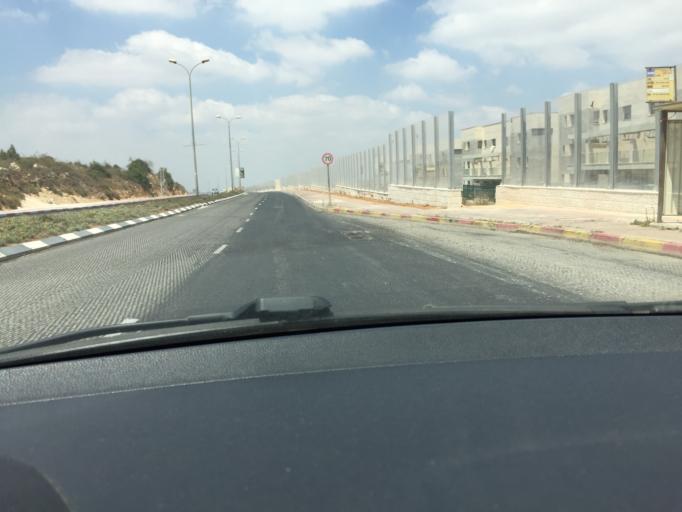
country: IL
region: Jerusalem
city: Ariel
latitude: 32.1038
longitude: 35.1866
